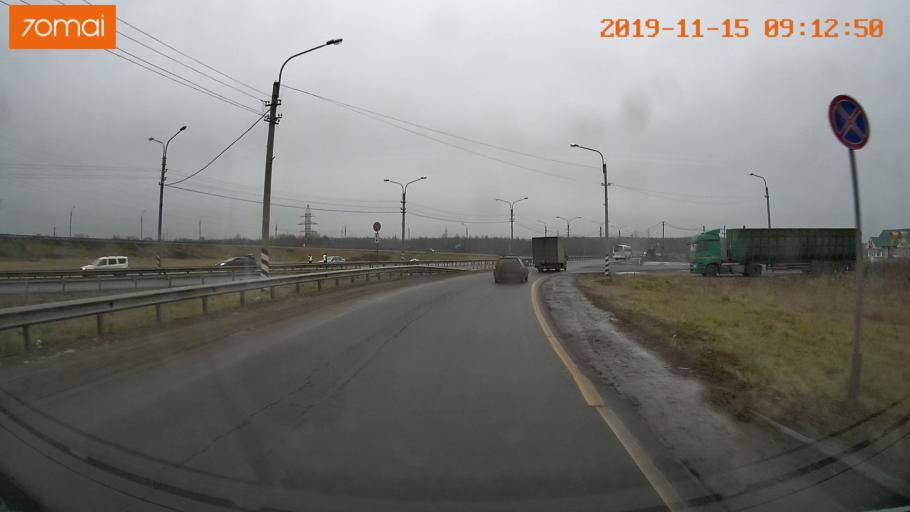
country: RU
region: Vologda
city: Tonshalovo
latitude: 59.2100
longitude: 37.9357
